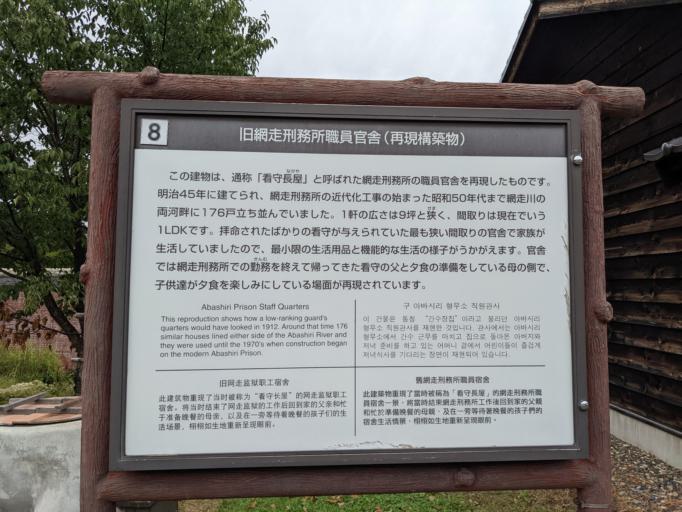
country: JP
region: Hokkaido
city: Abashiri
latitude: 43.9957
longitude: 144.2292
